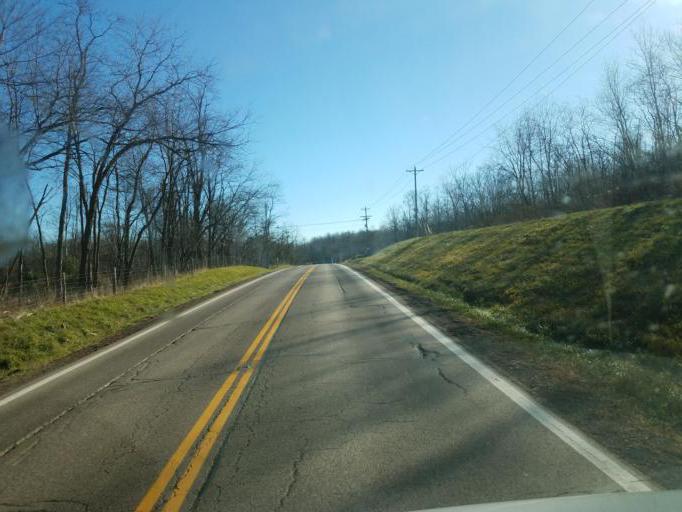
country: US
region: Ohio
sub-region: Knox County
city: Oak Hill
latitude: 40.3337
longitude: -82.2475
